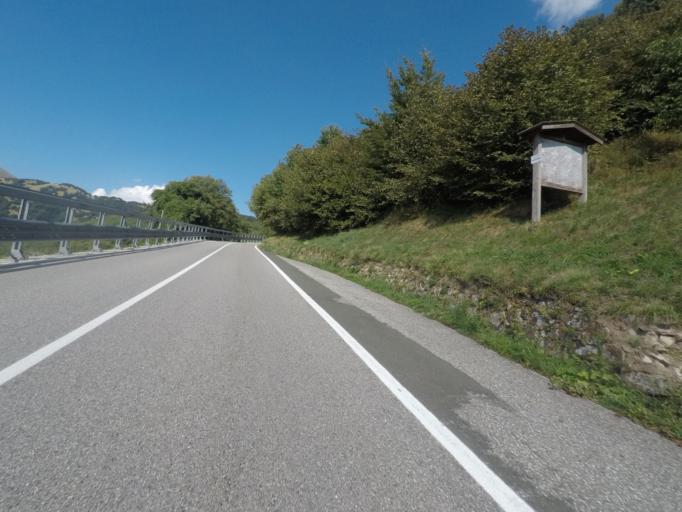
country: IT
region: Tuscany
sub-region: Provincia di Massa-Carrara
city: Comano
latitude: 44.2841
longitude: 10.1986
